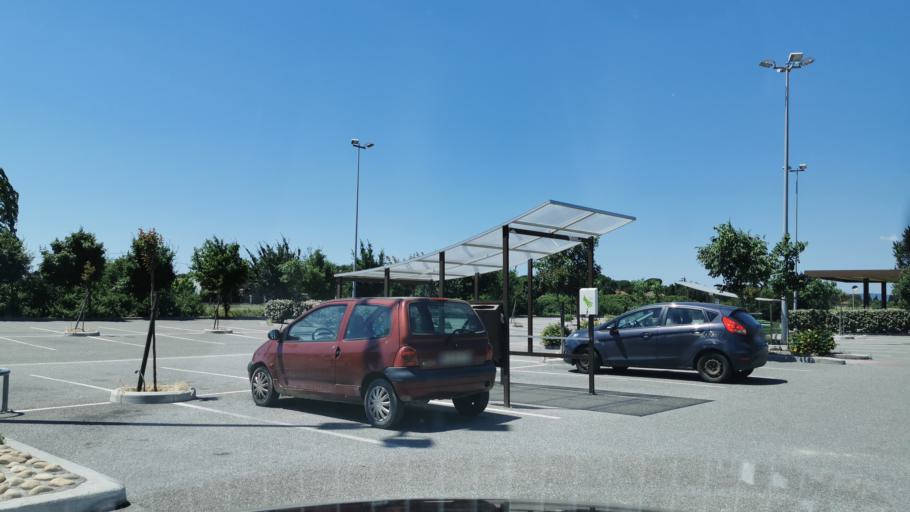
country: FR
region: Languedoc-Roussillon
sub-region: Departement de l'Aude
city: Saint-Marcel-sur-Aude
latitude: 43.2658
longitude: 2.9499
